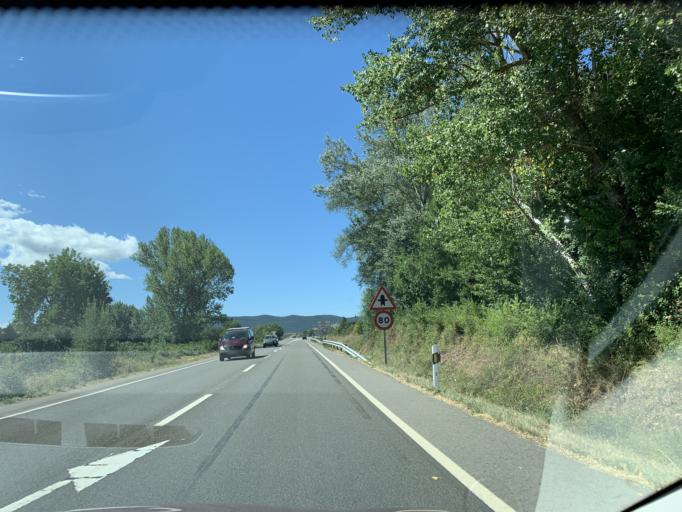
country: ES
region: Aragon
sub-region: Provincia de Huesca
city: Sabinanigo
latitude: 42.5523
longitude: -0.3429
